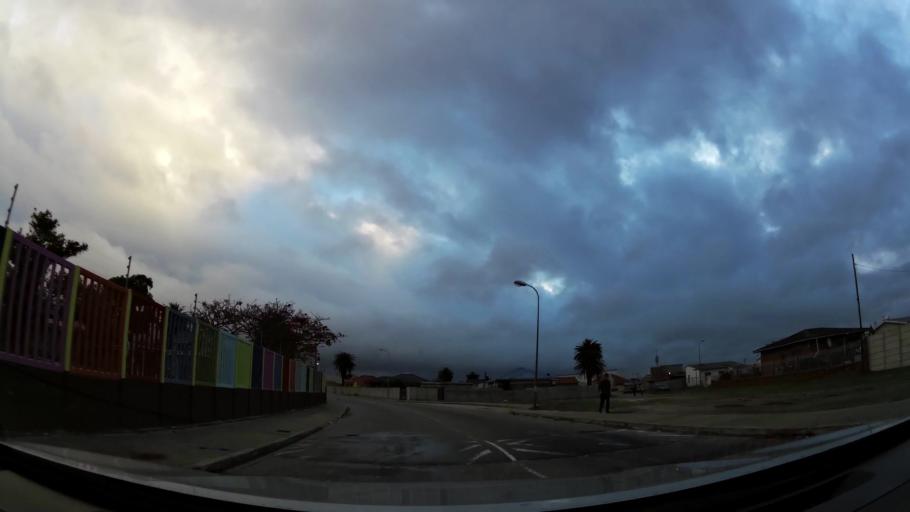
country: ZA
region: Eastern Cape
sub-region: Nelson Mandela Bay Metropolitan Municipality
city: Port Elizabeth
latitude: -33.9255
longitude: 25.6012
